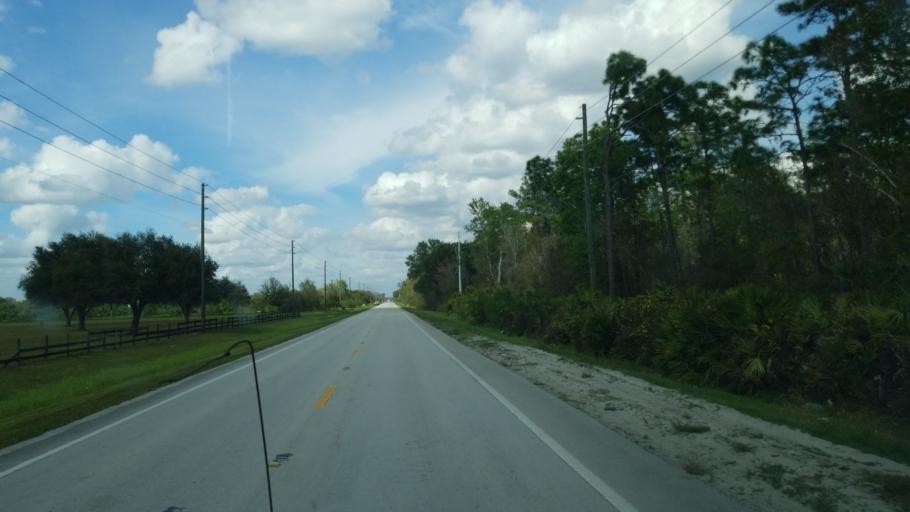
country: US
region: Florida
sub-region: Osceola County
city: Saint Cloud
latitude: 28.1162
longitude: -81.0763
